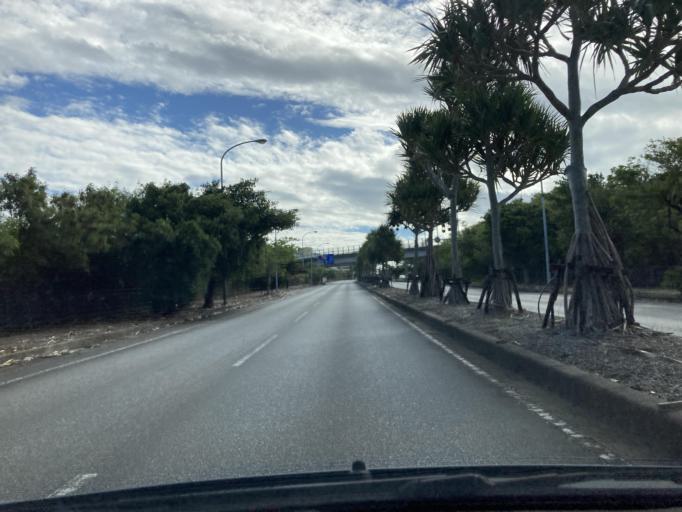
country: JP
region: Okinawa
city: Tomigusuku
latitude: 26.1673
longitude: 127.7258
